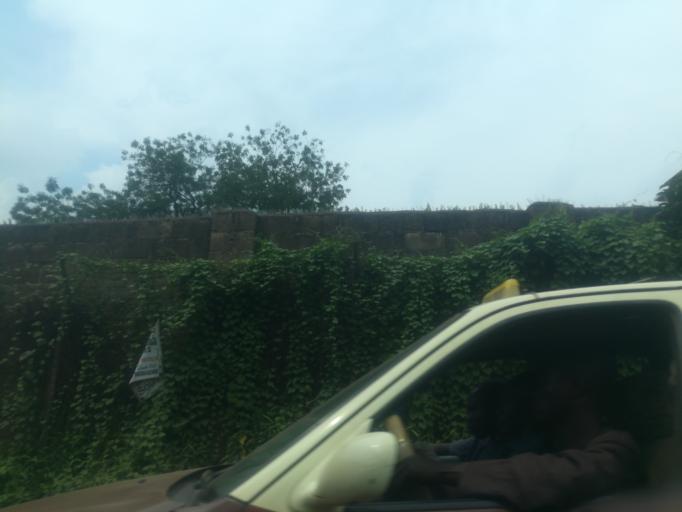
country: NG
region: Oyo
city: Ibadan
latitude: 7.4298
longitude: 3.9140
